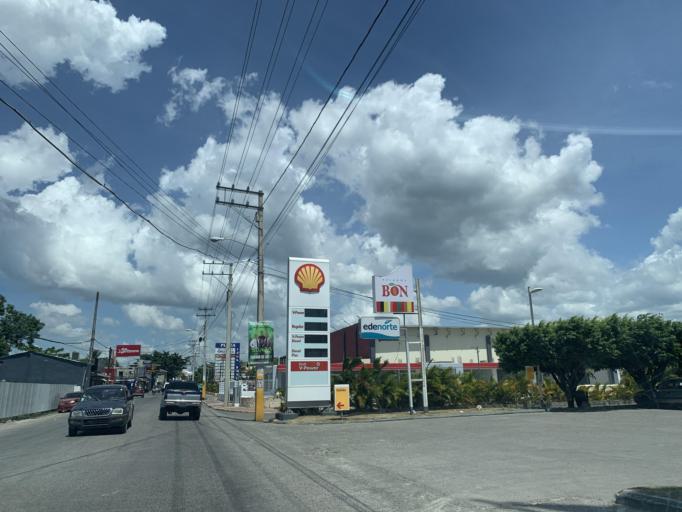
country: DO
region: Espaillat
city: Jamao al Norte
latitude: 19.6701
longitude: -70.3701
